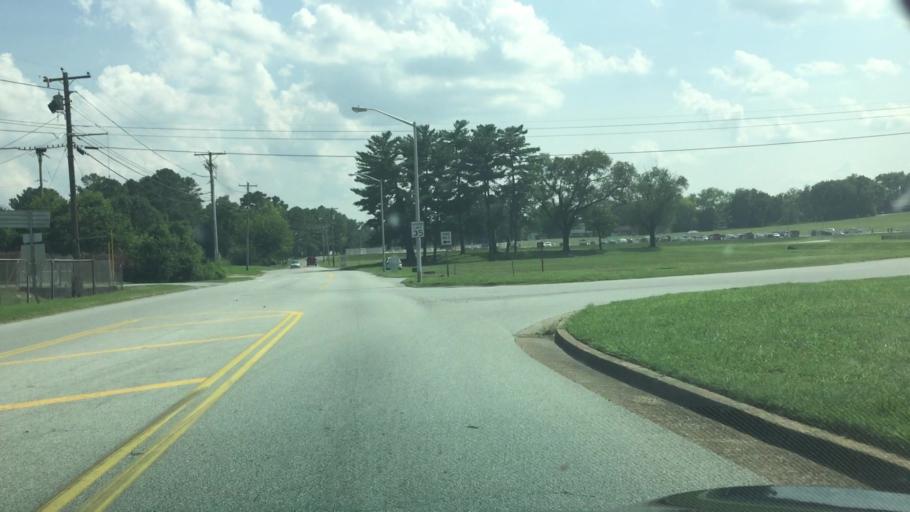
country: US
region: Tennessee
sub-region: Hamilton County
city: East Brainerd
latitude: 35.0334
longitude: -85.1945
